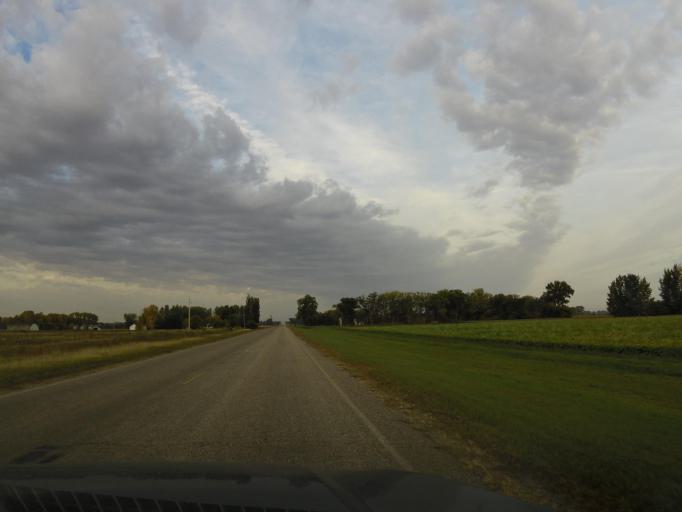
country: US
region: North Dakota
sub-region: Pembina County
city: Cavalier
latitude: 48.6882
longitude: -97.6408
